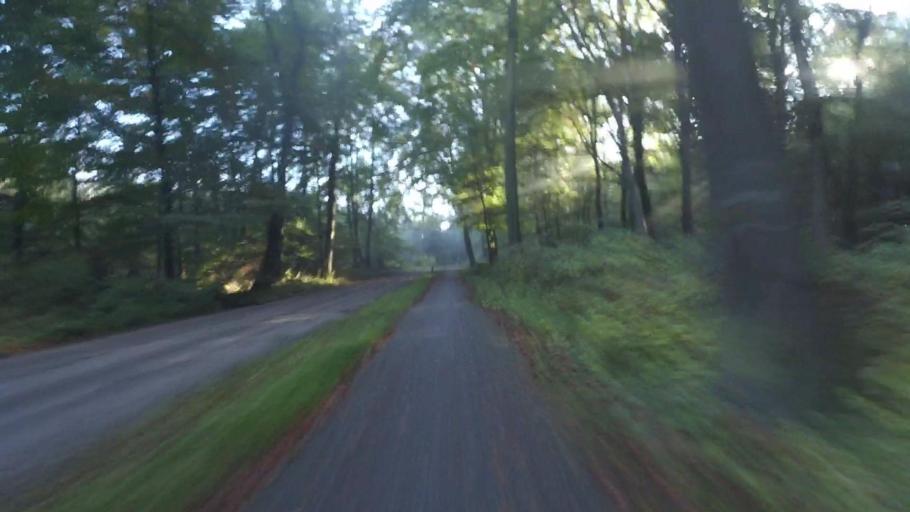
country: NL
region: Gelderland
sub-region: Gemeente Epe
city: Vaassen
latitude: 52.2881
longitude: 5.9209
